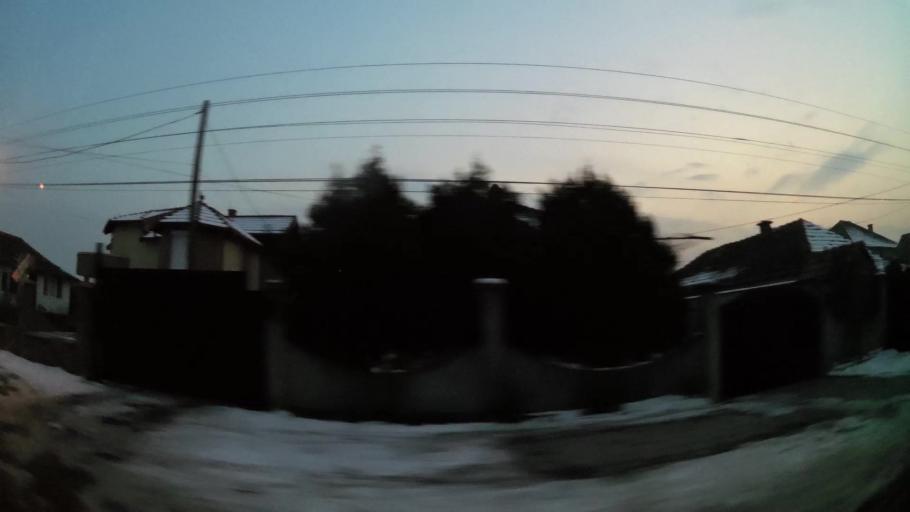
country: MK
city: Creshevo
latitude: 42.0033
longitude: 21.5181
